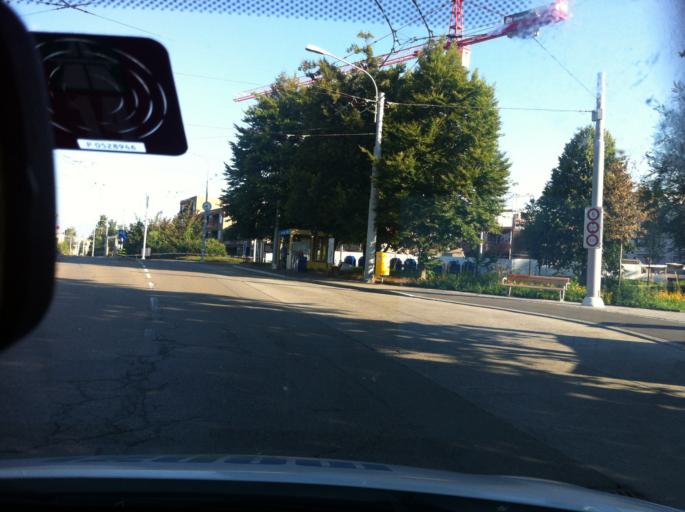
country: CH
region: Zurich
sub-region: Bezirk Meilen
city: Zollikerberg
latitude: 47.3547
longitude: 8.6012
